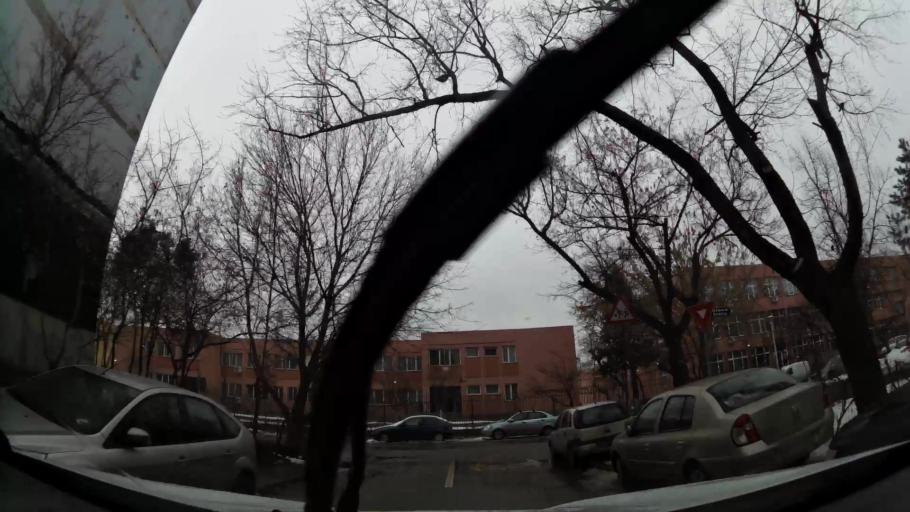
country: RO
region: Ilfov
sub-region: Comuna Chiajna
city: Rosu
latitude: 44.4131
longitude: 26.0174
